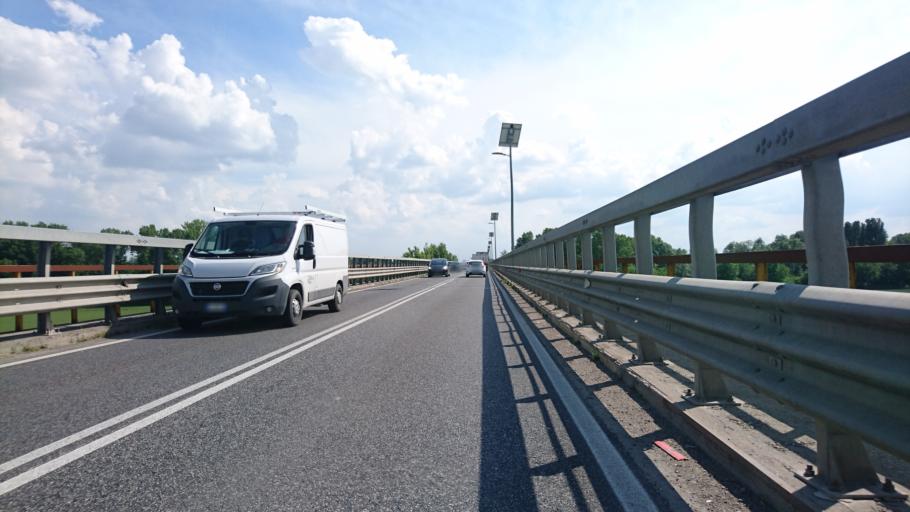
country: IT
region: Veneto
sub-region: Provincia di Rovigo
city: Castelnovo Bariano
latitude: 45.0198
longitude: 11.2918
